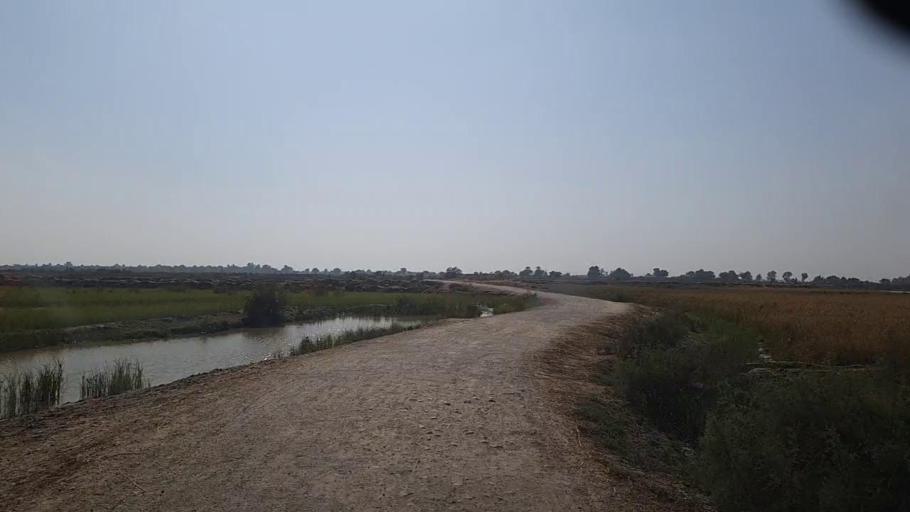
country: PK
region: Sindh
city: Thul
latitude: 28.1770
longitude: 68.7736
